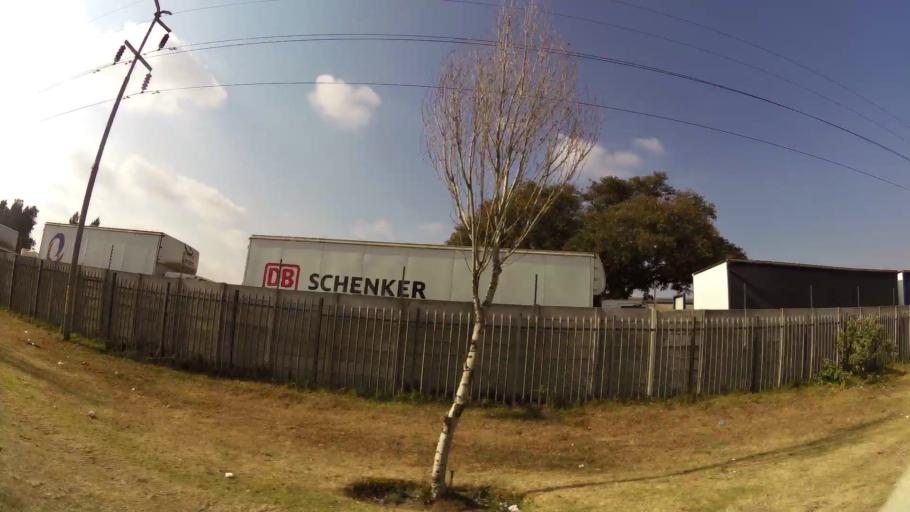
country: ZA
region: Gauteng
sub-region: Ekurhuleni Metropolitan Municipality
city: Boksburg
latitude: -26.1605
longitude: 28.2055
